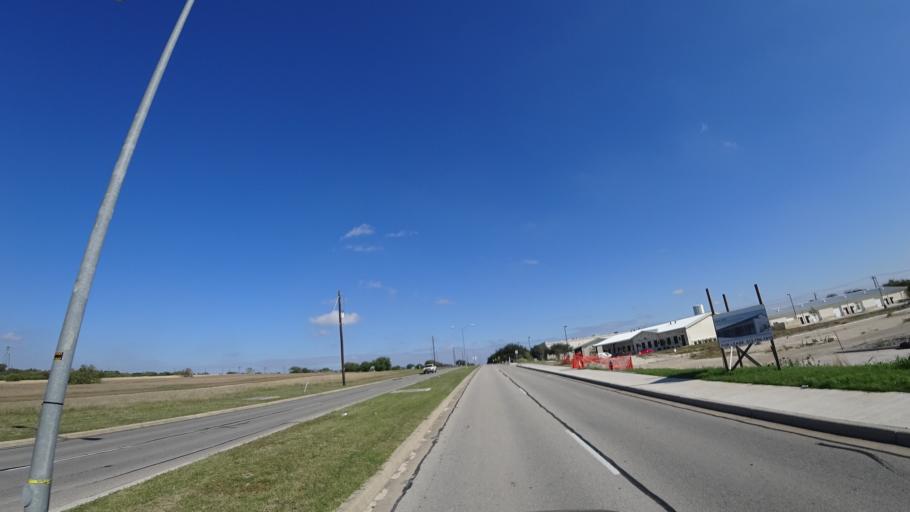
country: US
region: Texas
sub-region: Travis County
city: Windemere
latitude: 30.4364
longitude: -97.6474
